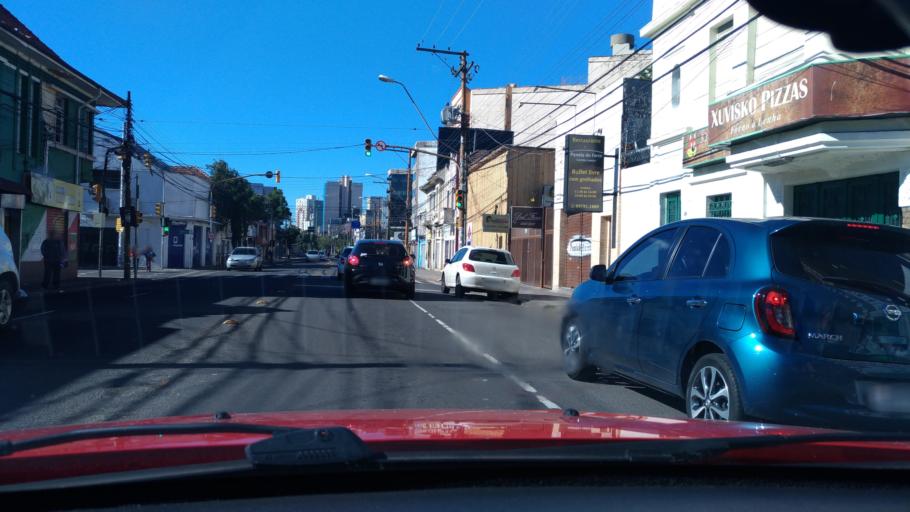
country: BR
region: Rio Grande do Sul
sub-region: Porto Alegre
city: Porto Alegre
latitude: -30.0231
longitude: -51.2096
